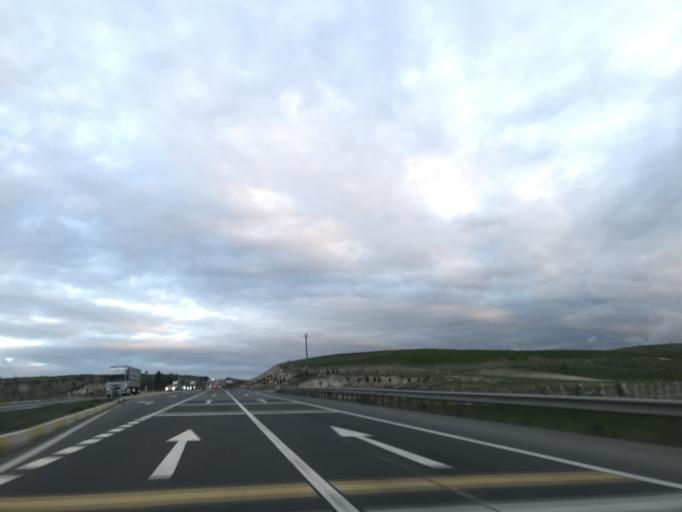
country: TR
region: Ankara
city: Ikizce
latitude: 39.5244
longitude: 32.8640
